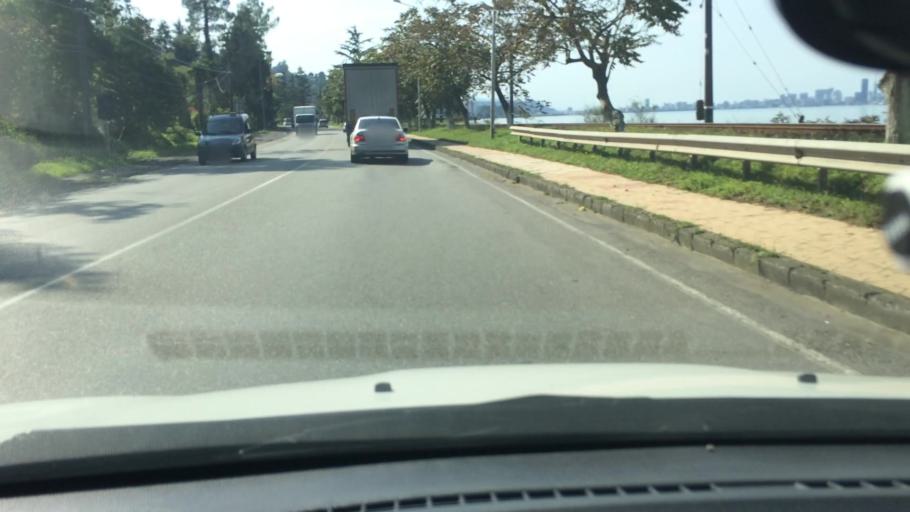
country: GE
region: Ajaria
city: Makhinjauri
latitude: 41.6826
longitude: 41.6994
